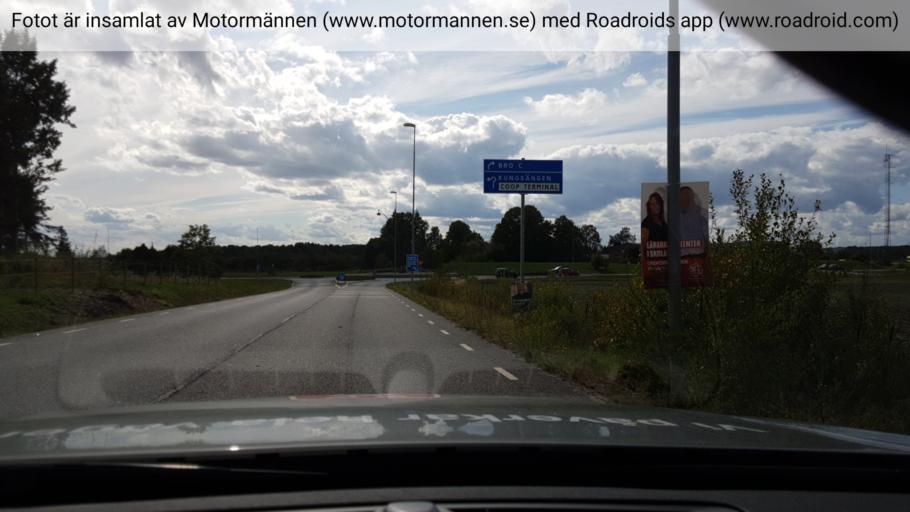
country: SE
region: Stockholm
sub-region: Upplands-Bro Kommun
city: Bro
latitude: 59.5072
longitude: 17.6631
